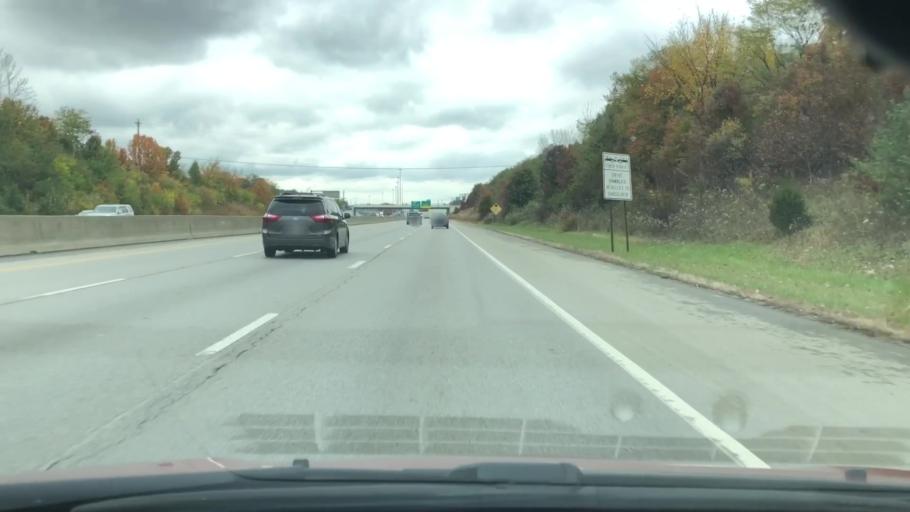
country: US
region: Ohio
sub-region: Franklin County
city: Huber Ridge
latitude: 40.0799
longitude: -82.8717
